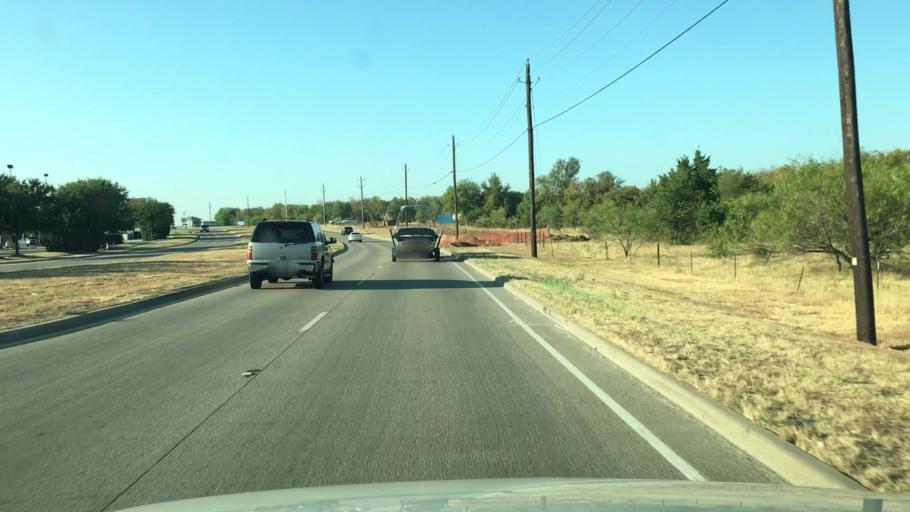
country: US
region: Texas
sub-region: Johnson County
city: Burleson
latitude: 32.5265
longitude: -97.3526
